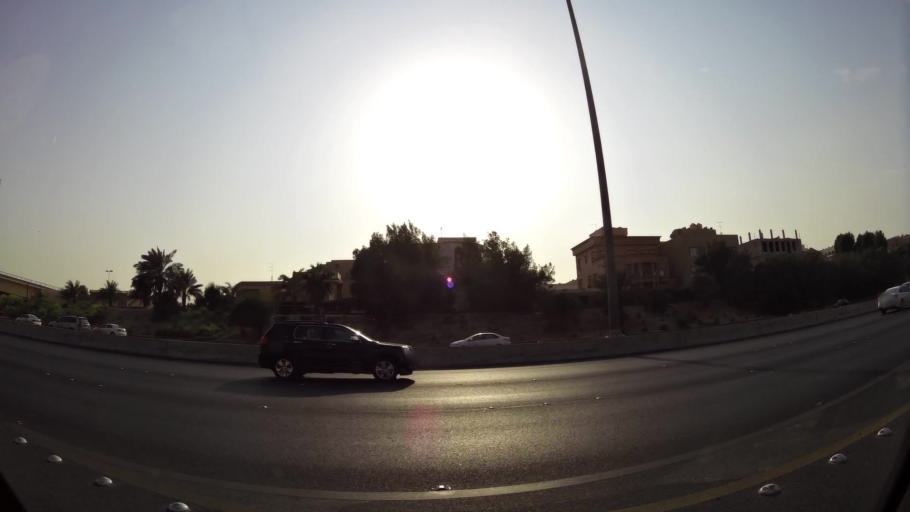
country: KW
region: Muhafazat Hawalli
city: Hawalli
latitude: 29.3200
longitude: 48.0146
